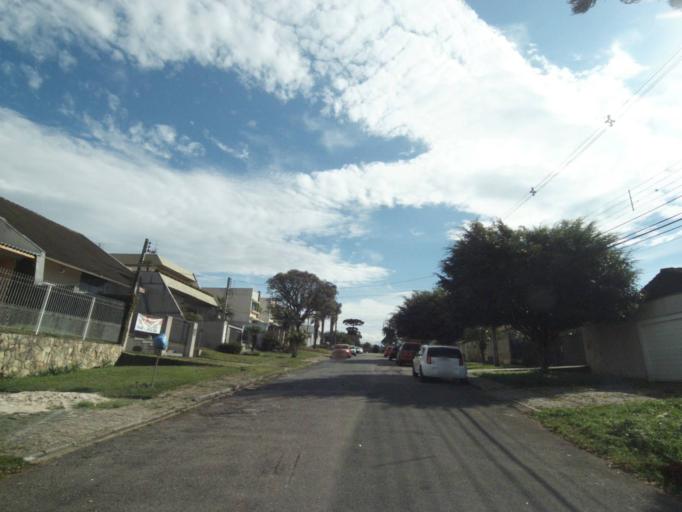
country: BR
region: Parana
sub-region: Curitiba
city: Curitiba
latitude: -25.4099
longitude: -49.2807
